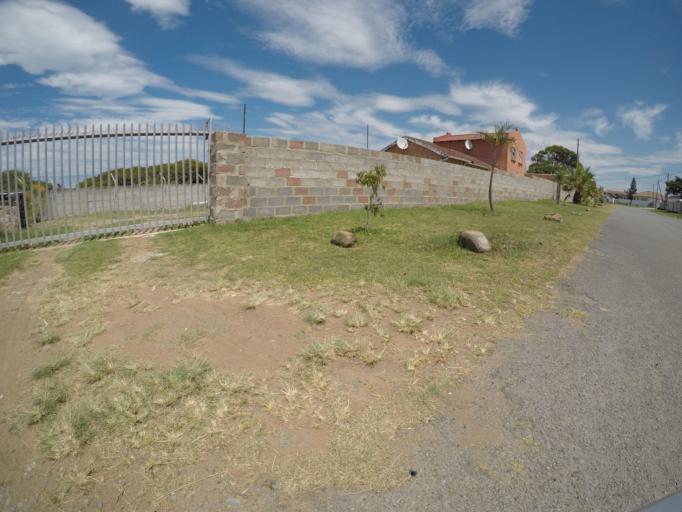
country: ZA
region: Eastern Cape
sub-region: Buffalo City Metropolitan Municipality
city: East London
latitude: -33.0441
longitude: 27.8685
